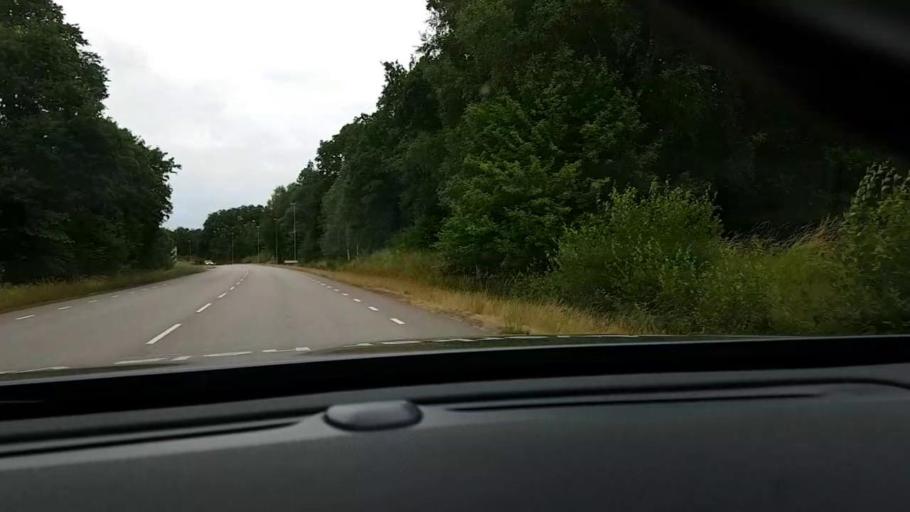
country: SE
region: Skane
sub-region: Hassleholms Kommun
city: Hassleholm
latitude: 56.1675
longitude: 13.7456
